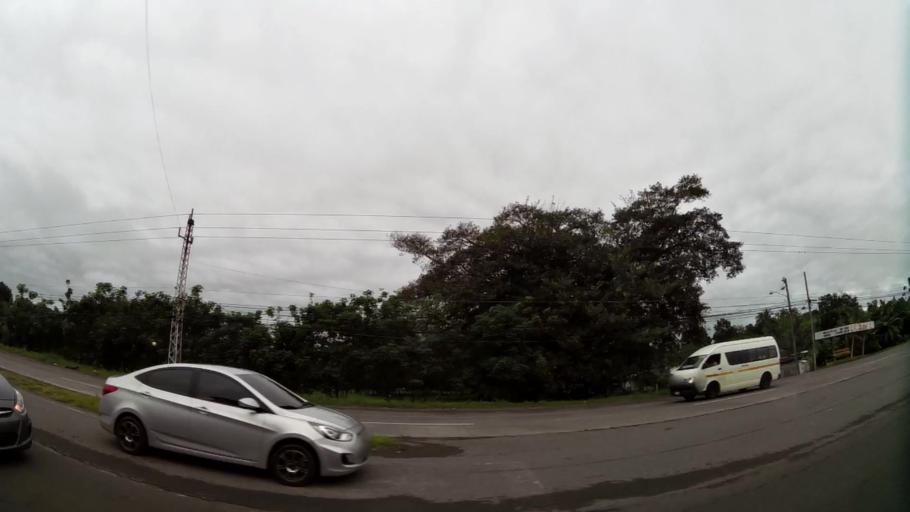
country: PA
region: Chiriqui
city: Boqueron
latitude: 8.4879
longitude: -82.5718
